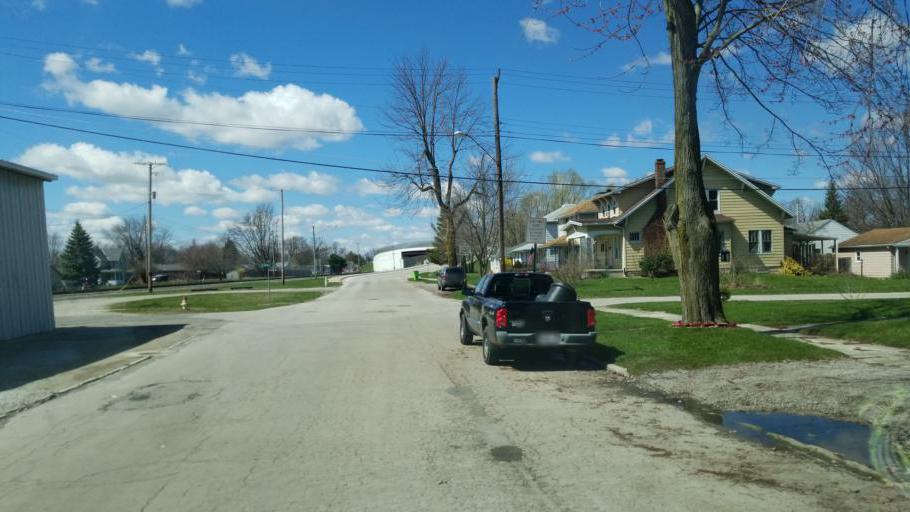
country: US
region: Ohio
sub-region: Seneca County
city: Fostoria
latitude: 41.1562
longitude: -83.4284
